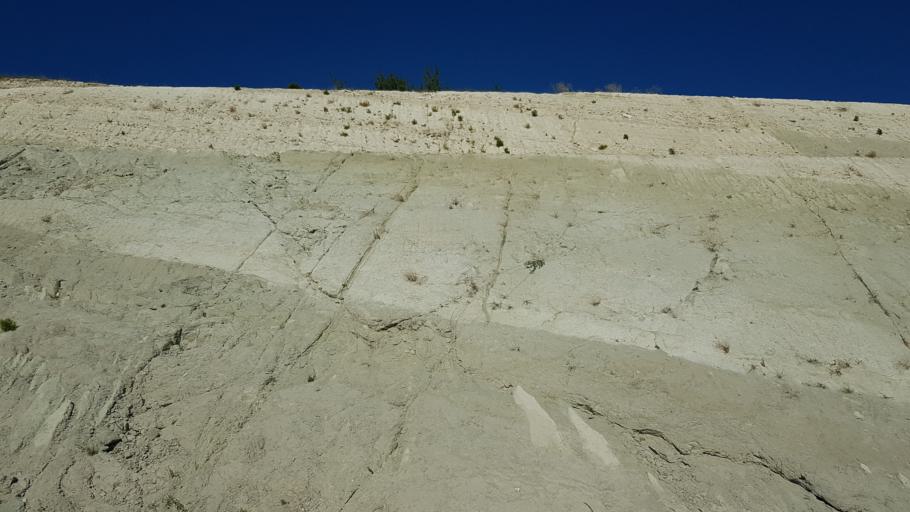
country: TR
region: Balikesir
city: Ertugrul
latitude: 39.5663
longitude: 27.7025
